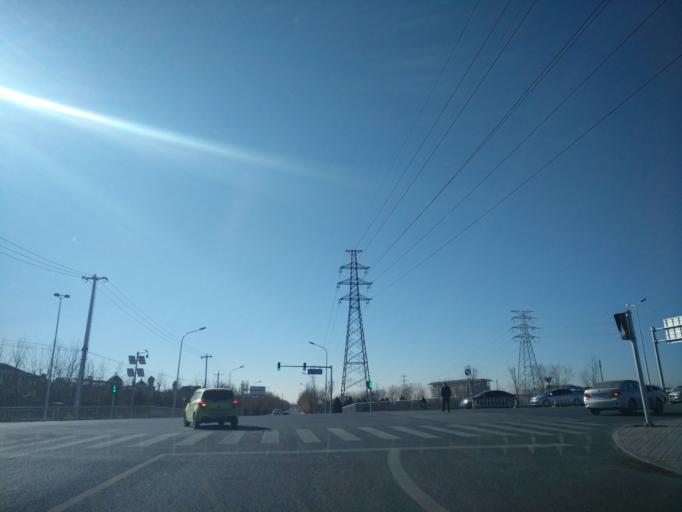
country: CN
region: Beijing
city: Qingyundian
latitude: 39.7525
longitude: 116.5313
